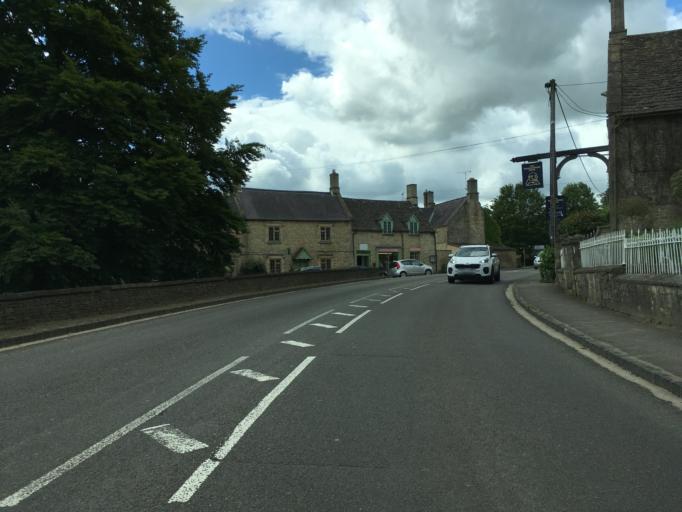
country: GB
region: England
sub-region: Oxfordshire
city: Shipton under Wychwood
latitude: 51.8588
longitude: -1.5968
